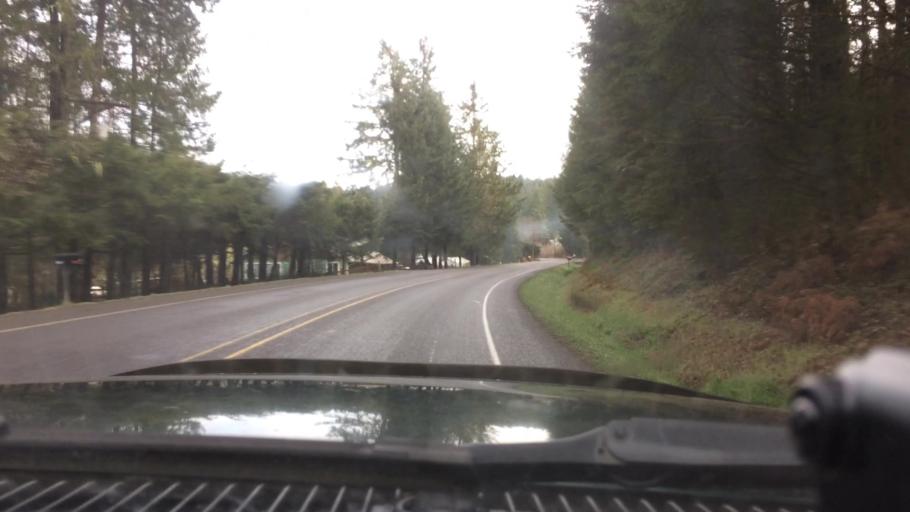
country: US
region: Oregon
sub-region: Lane County
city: Veneta
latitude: 44.1274
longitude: -123.3488
